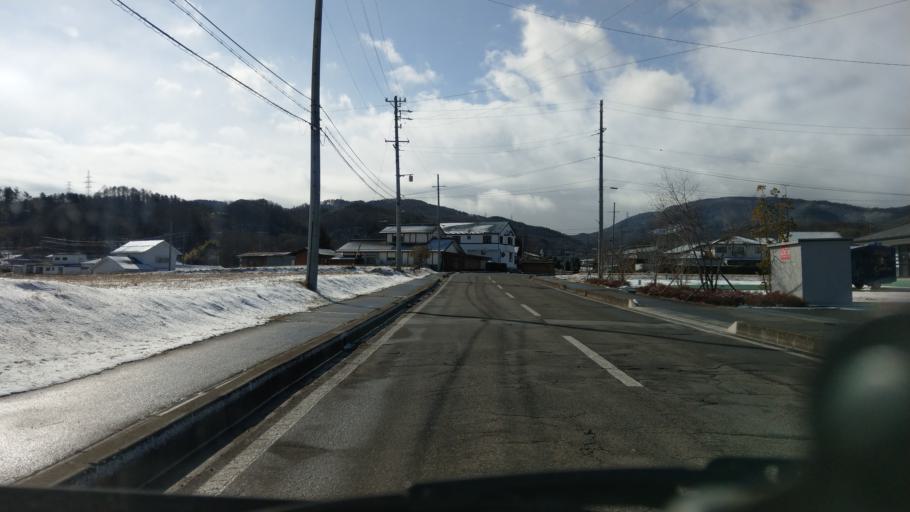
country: JP
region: Nagano
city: Kamimaruko
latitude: 36.2738
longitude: 138.3215
